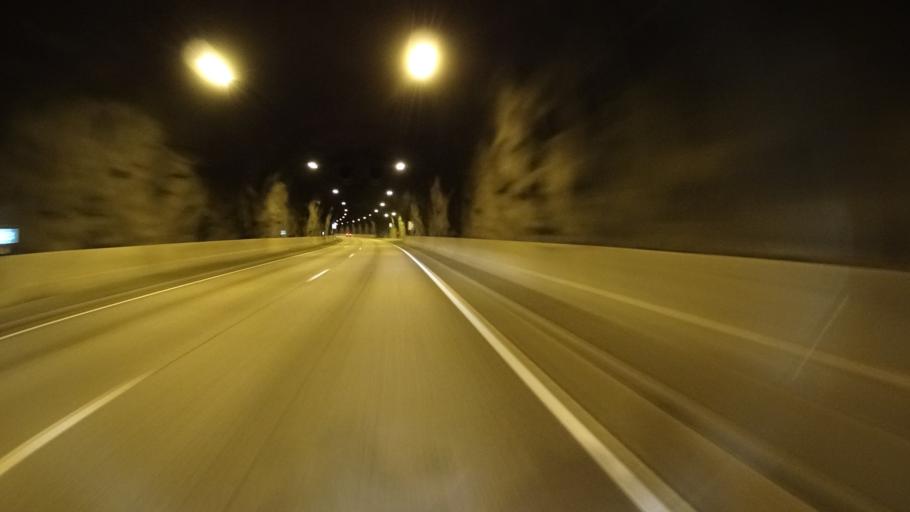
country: FI
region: Uusimaa
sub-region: Helsinki
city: Vantaa
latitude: 60.2378
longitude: 25.1602
